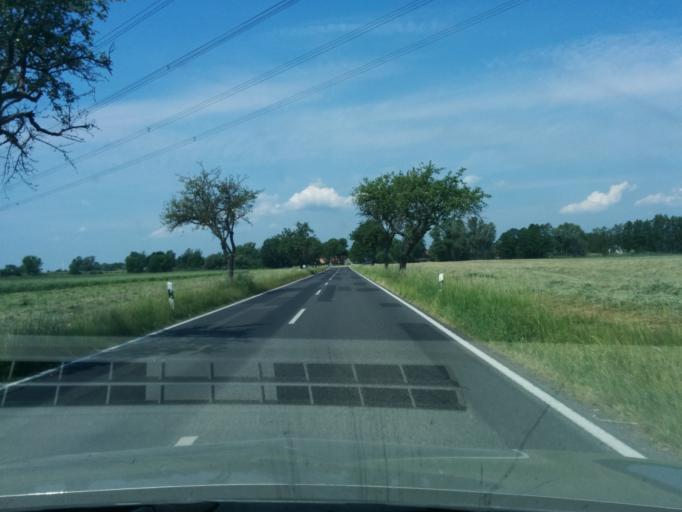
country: DE
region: Brandenburg
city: Ahrensfelde
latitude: 52.6215
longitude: 13.5800
